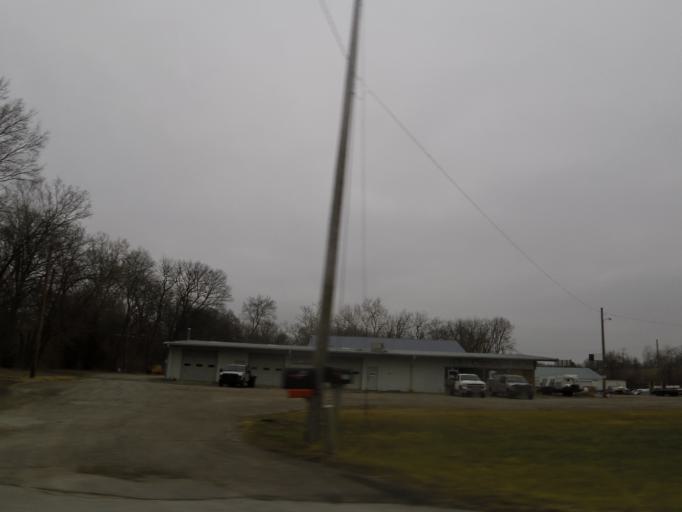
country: US
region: Missouri
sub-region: Marion County
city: Hannibal
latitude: 39.7155
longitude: -91.4006
